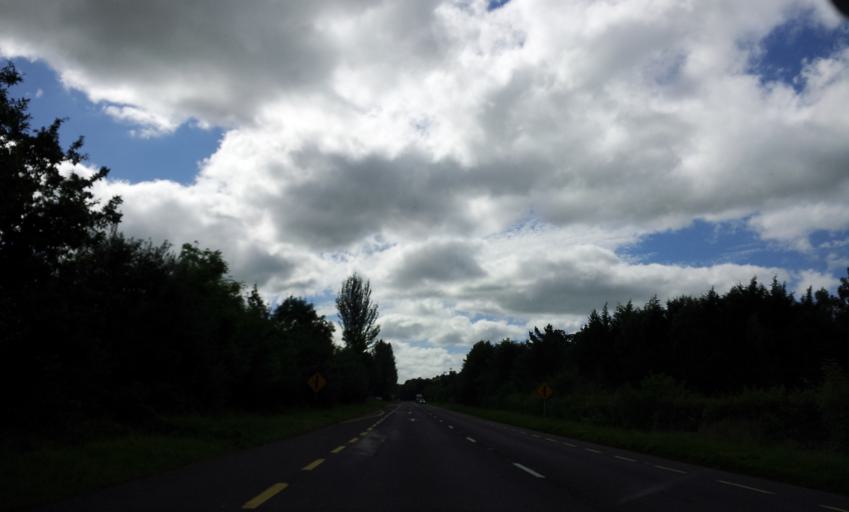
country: IE
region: Munster
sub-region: County Cork
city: Bandon
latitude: 51.8595
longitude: -8.7933
